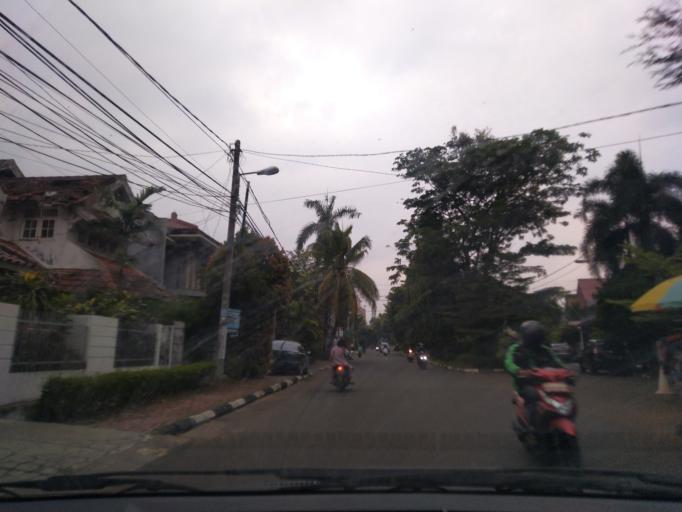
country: ID
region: Banten
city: South Tangerang
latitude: -6.2679
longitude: 106.7451
